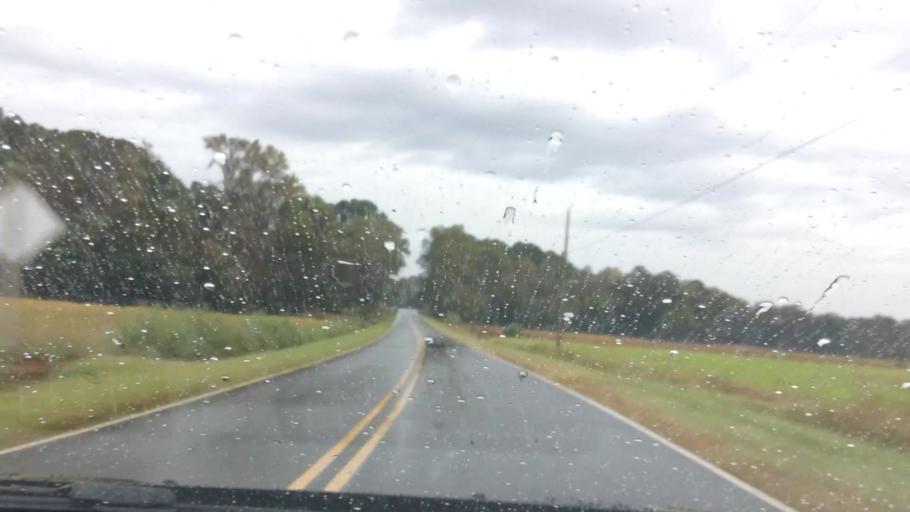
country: US
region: North Carolina
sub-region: Pitt County
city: Grifton
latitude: 35.3828
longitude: -77.4126
